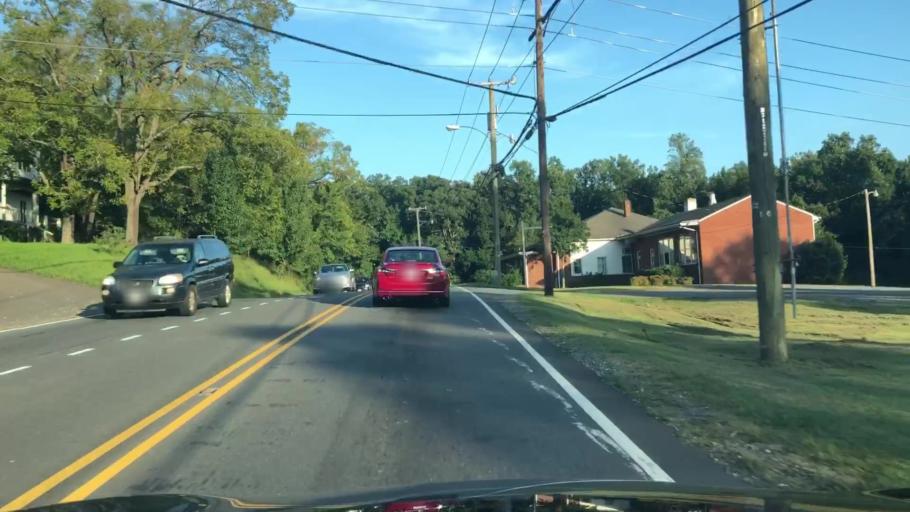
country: US
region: Virginia
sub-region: Stafford County
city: Falmouth
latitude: 38.3227
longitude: -77.4655
